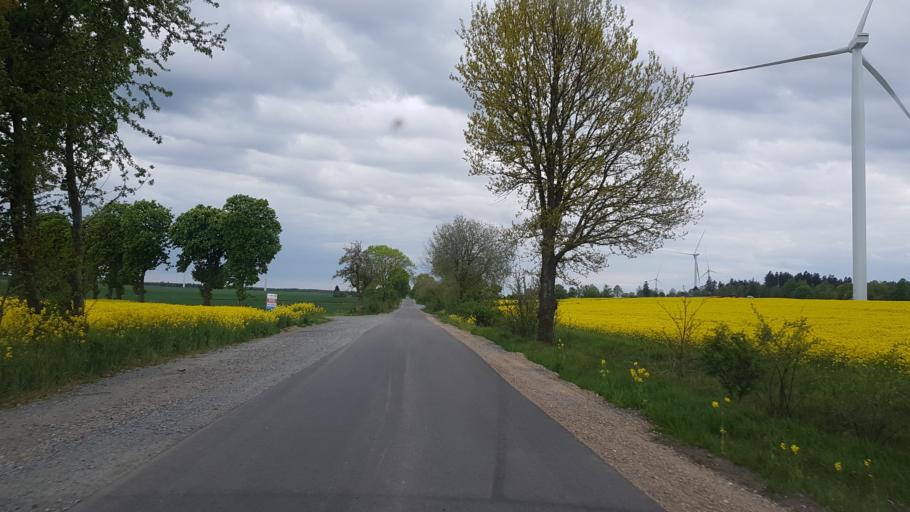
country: PL
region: West Pomeranian Voivodeship
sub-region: Powiat slawienski
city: Slawno
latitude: 54.2569
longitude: 16.5504
